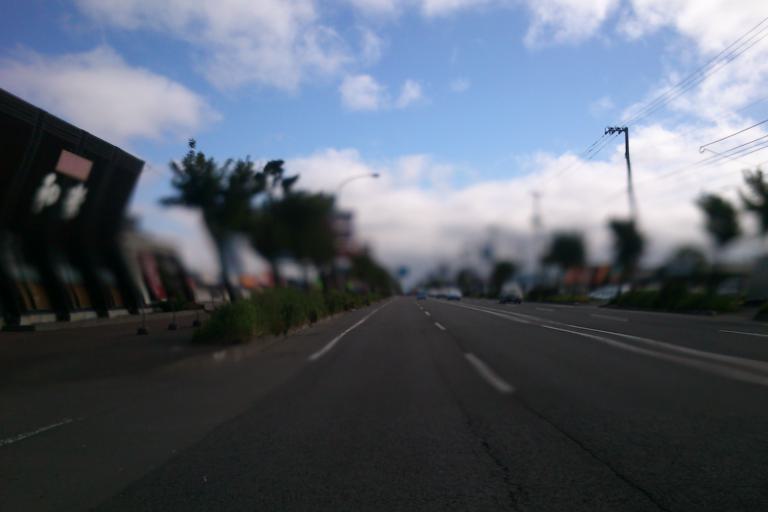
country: JP
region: Hokkaido
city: Sapporo
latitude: 43.1426
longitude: 141.2755
